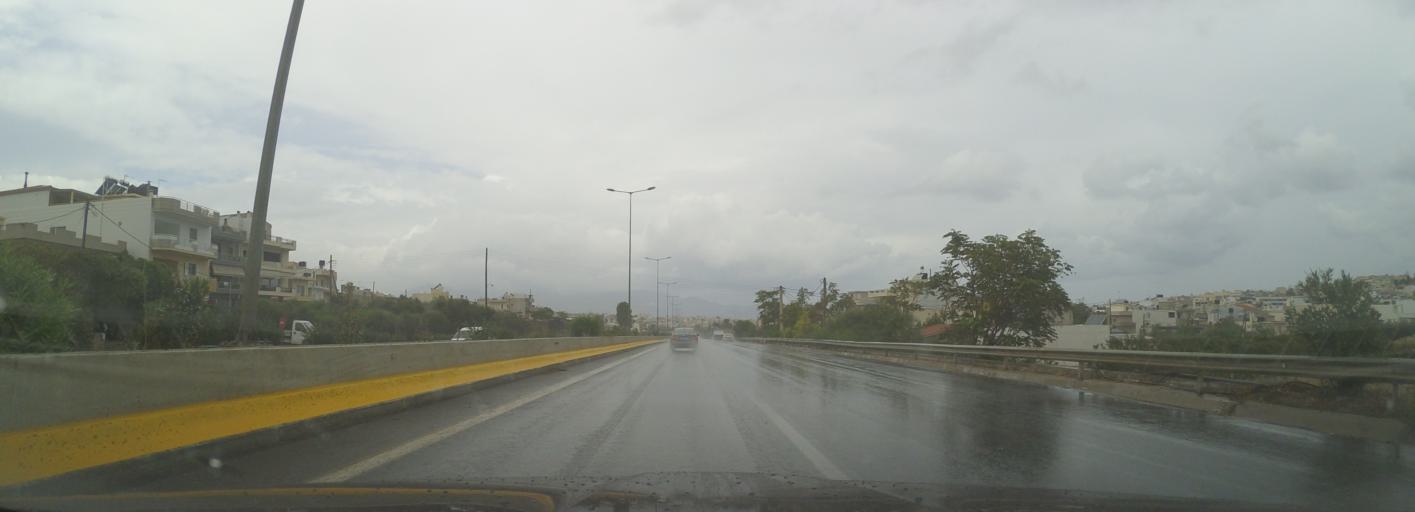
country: GR
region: Crete
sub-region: Nomos Irakleiou
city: Irakleion
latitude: 35.3201
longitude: 25.1193
